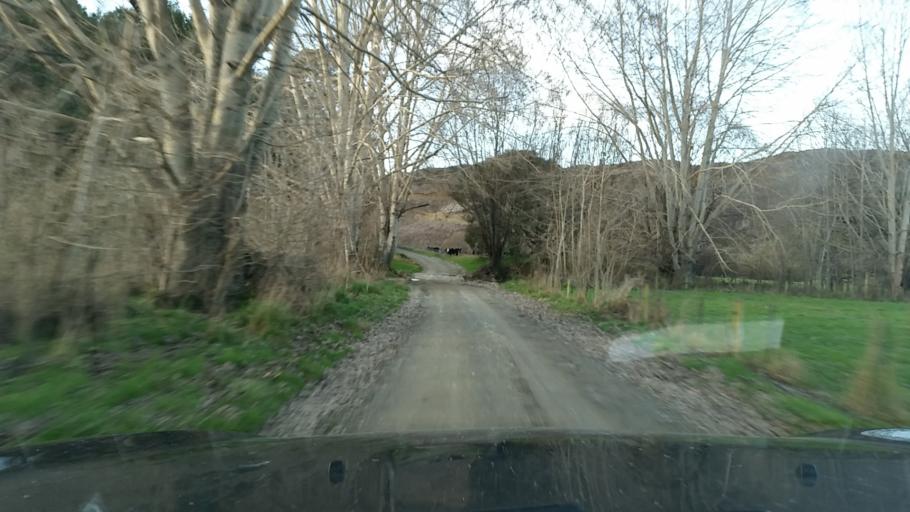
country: NZ
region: Marlborough
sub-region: Marlborough District
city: Blenheim
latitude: -41.5087
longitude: 173.5910
